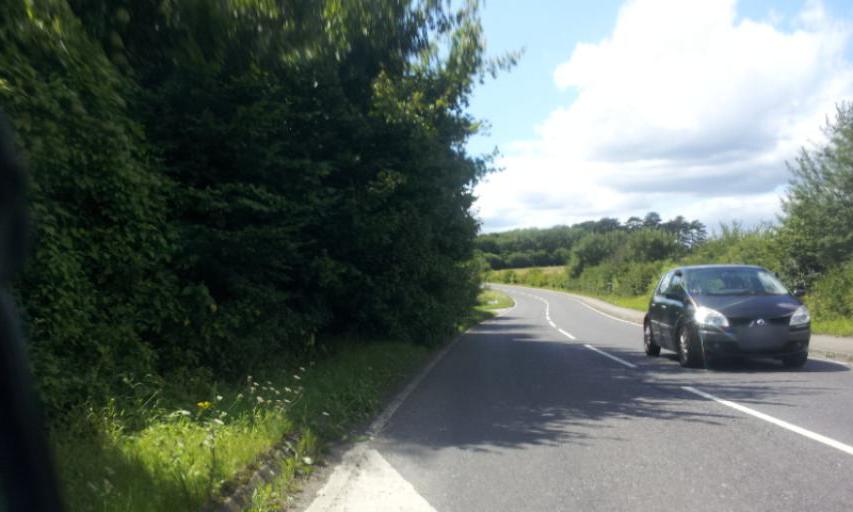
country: GB
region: England
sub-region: Kent
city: Boxley
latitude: 51.3002
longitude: 0.5408
